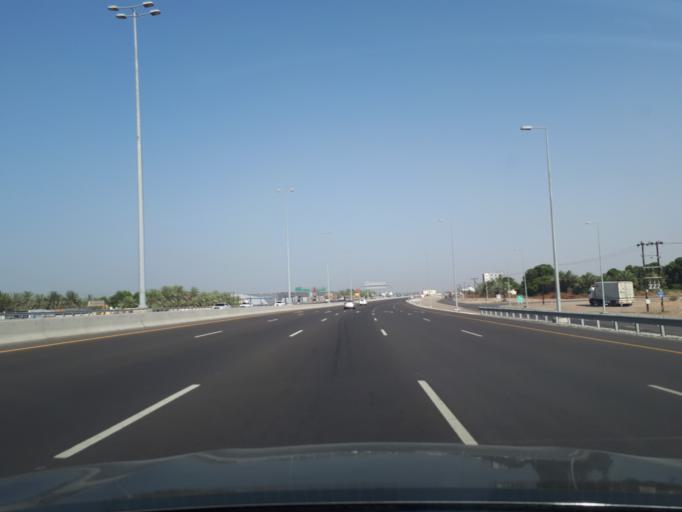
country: OM
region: Al Batinah
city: Al Liwa'
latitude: 24.4189
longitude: 56.6245
